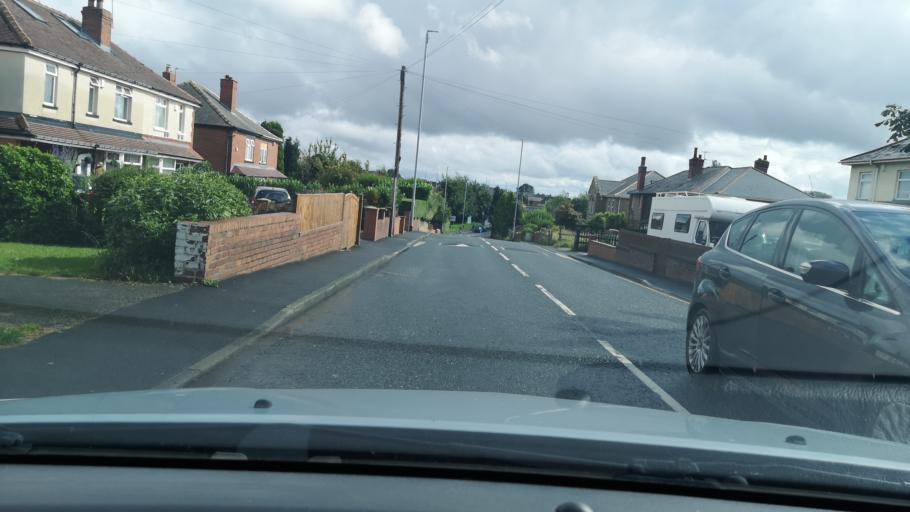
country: GB
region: England
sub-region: City and Borough of Leeds
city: Morley
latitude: 53.7273
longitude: -1.5860
